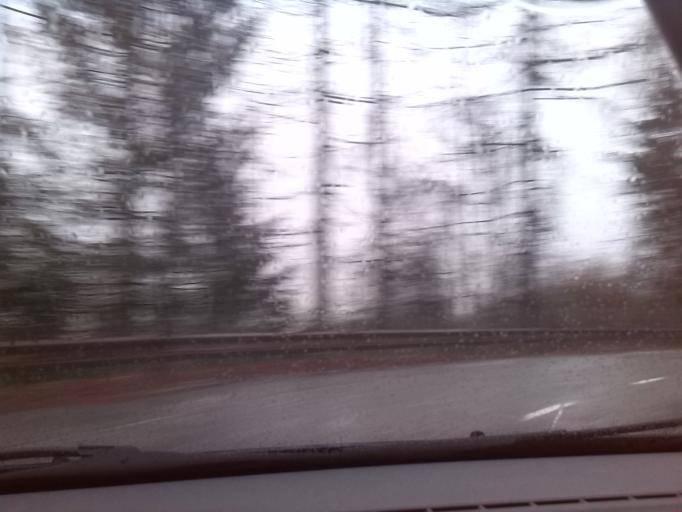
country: SI
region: Kobarid
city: Kobarid
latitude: 46.2252
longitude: 13.5898
